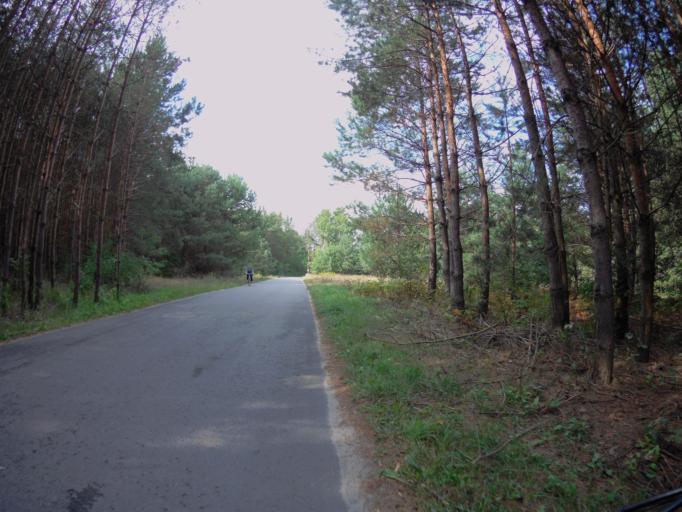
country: PL
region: Subcarpathian Voivodeship
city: Nowa Sarzyna
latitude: 50.2980
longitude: 22.3501
